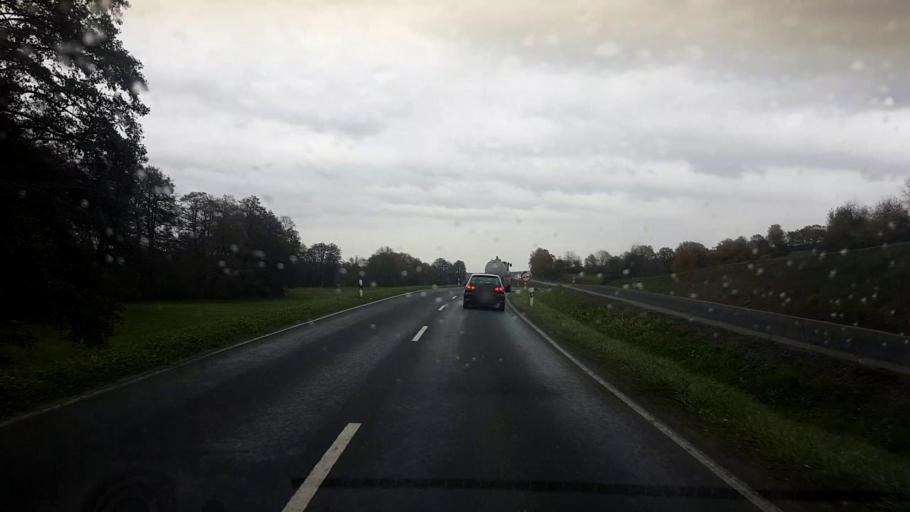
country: DE
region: Bavaria
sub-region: Upper Franconia
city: Burgwindheim
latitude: 49.8785
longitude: 10.6064
